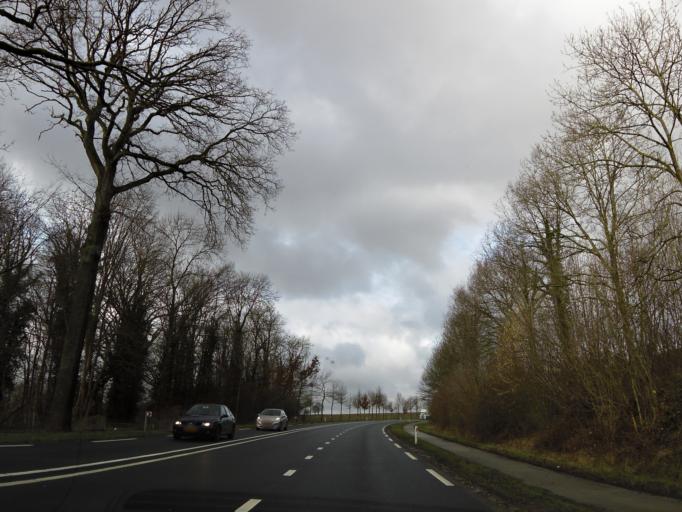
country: NL
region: Limburg
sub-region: Valkenburg aan de Geul
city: Schin op Geul
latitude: 50.8103
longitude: 5.8722
